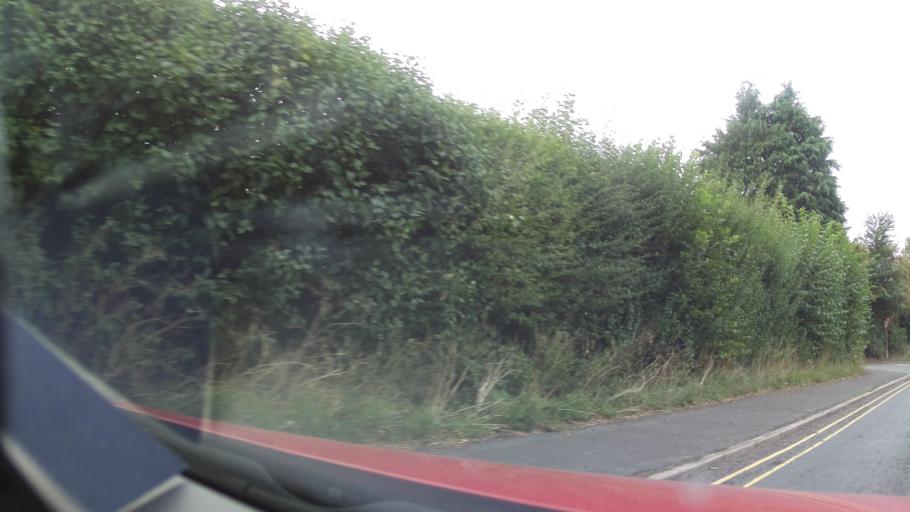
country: GB
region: England
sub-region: Shropshire
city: Bridgnorth
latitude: 52.5384
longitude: -2.4103
